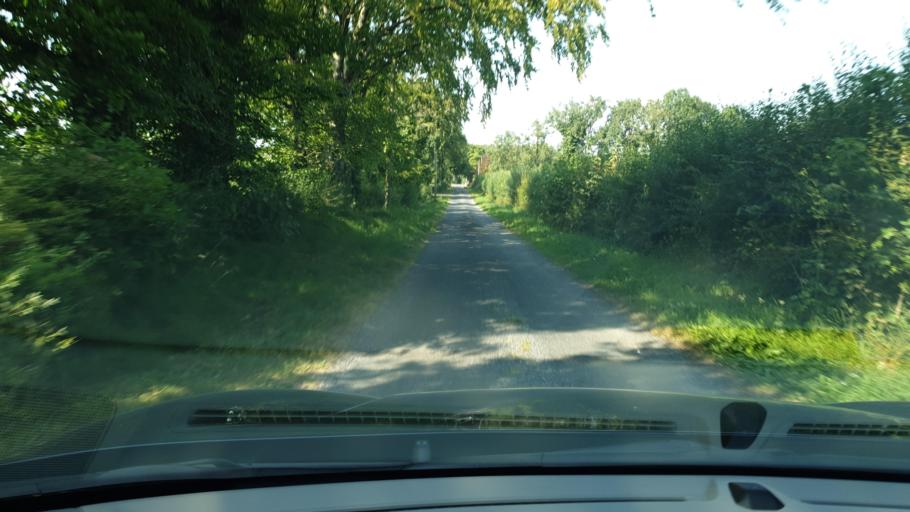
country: IE
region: Leinster
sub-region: An Mhi
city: Athboy
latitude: 53.6144
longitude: -6.9925
